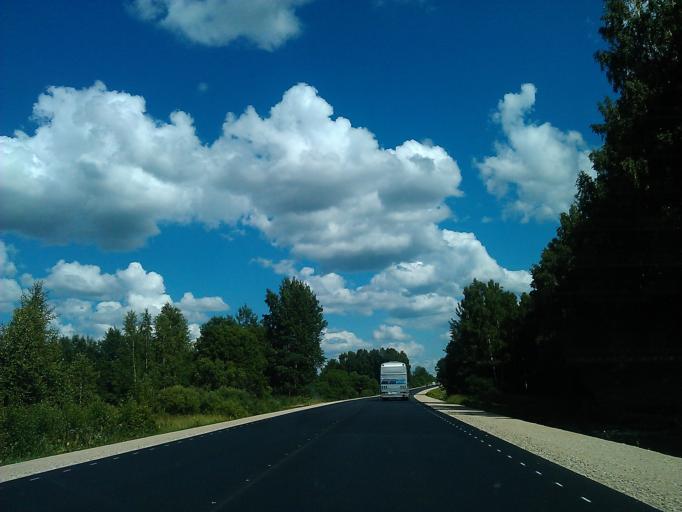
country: LV
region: Rezekne
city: Rezekne
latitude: 56.5340
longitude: 27.2412
